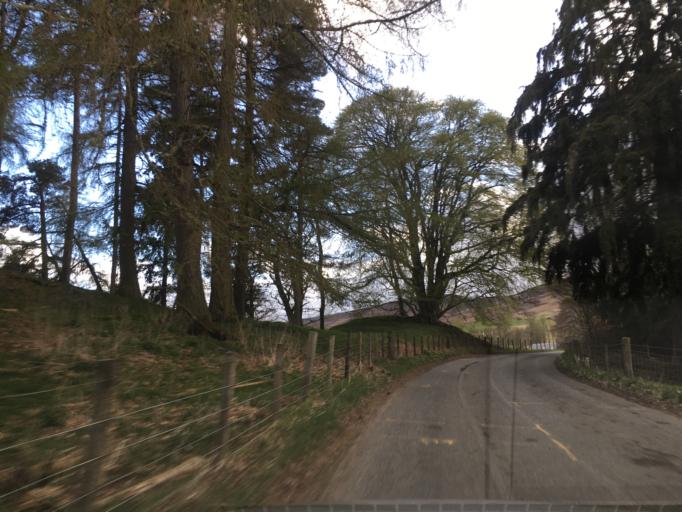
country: GB
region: Scotland
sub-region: Perth and Kinross
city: Aberfeldy
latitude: 56.7552
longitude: -4.0832
